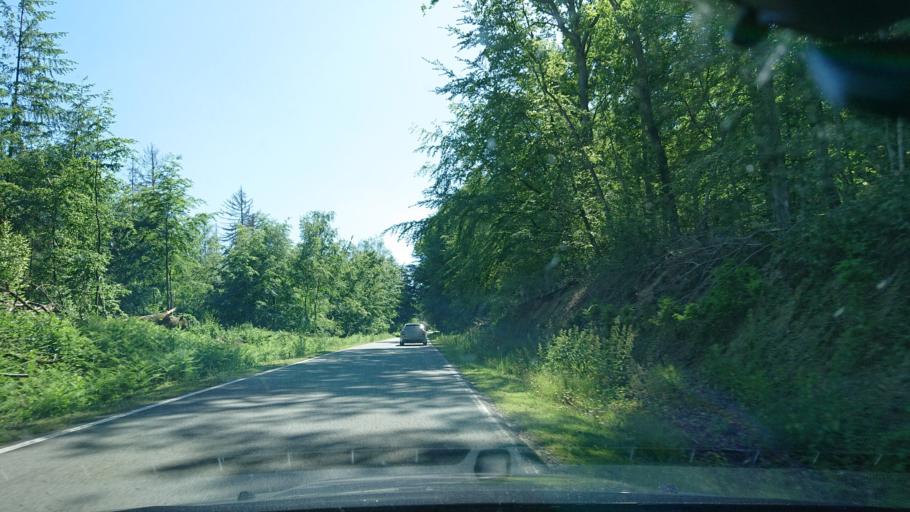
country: DE
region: North Rhine-Westphalia
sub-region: Regierungsbezirk Arnsberg
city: Mohnesee
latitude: 51.4751
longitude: 8.1553
